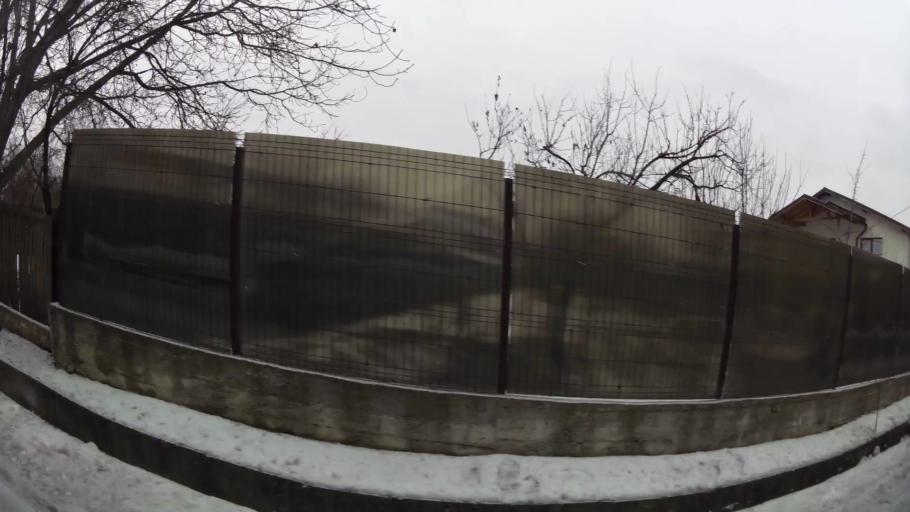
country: RO
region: Dambovita
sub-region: Comuna Aninoasa
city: Viforata
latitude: 44.9430
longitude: 25.4724
